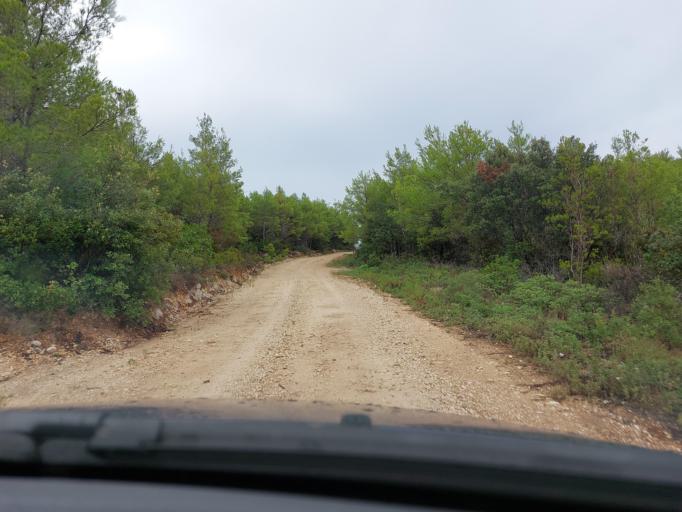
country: HR
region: Dubrovacko-Neretvanska
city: Smokvica
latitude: 42.7465
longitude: 16.9164
